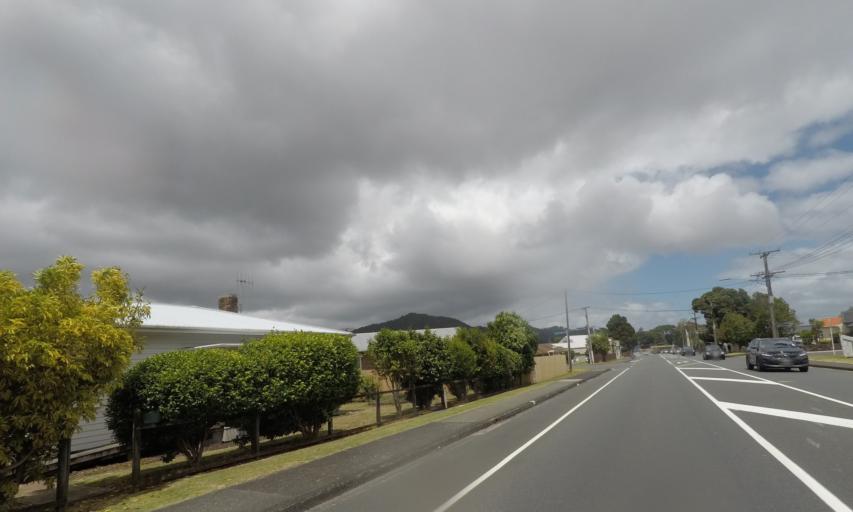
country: NZ
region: Northland
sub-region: Whangarei
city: Whangarei
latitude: -35.7060
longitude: 174.3198
